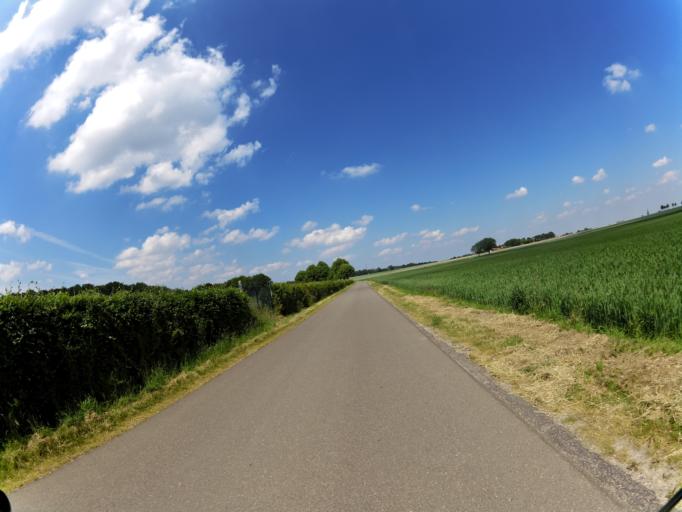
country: NL
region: Limburg
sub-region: Gemeente Kerkrade
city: Kerkrade
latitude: 50.9110
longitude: 6.0704
